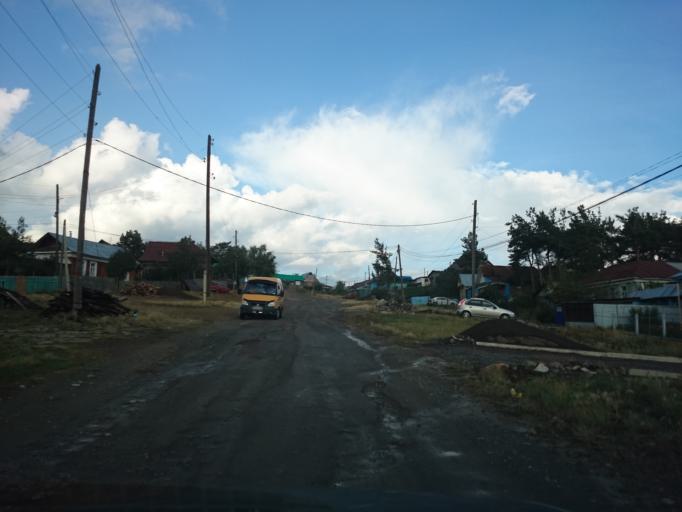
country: RU
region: Bashkortostan
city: Beloretsk
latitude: 53.9659
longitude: 58.3511
